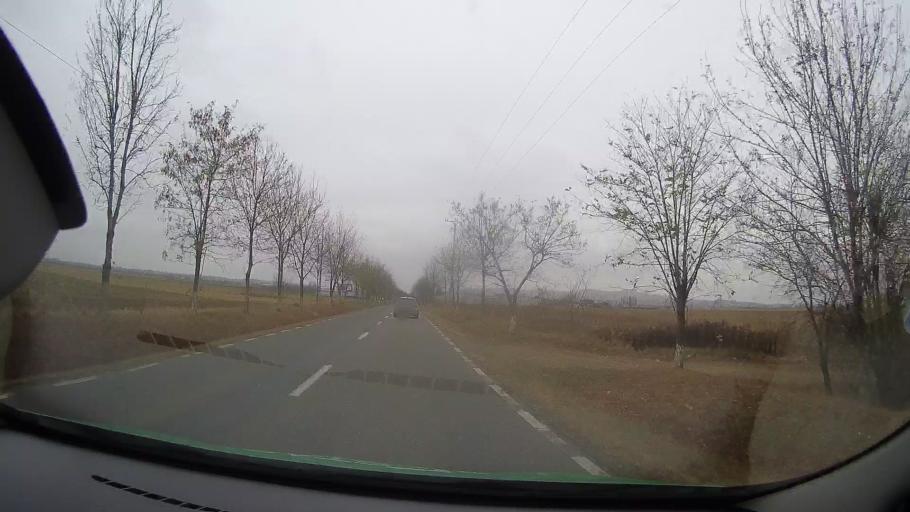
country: RO
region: Prahova
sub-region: Oras Baicoi
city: Liliesti
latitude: 45.0123
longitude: 25.8846
